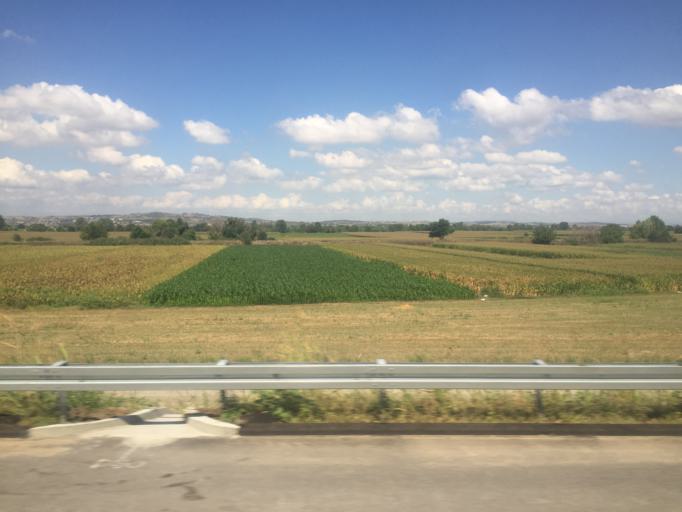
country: TR
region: Balikesir
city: Gobel
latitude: 40.0185
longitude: 28.2028
